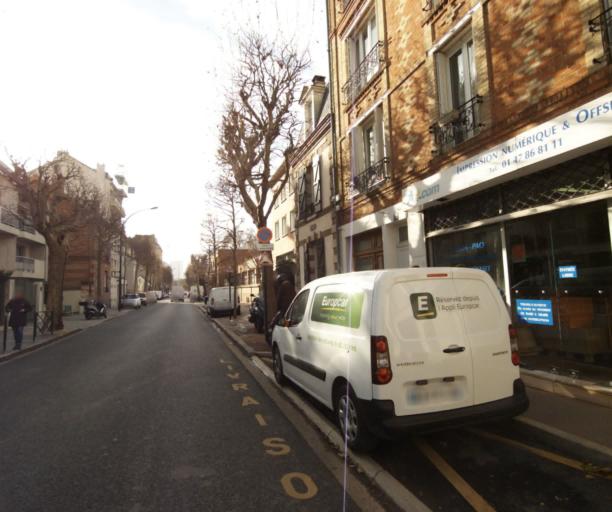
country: FR
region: Ile-de-France
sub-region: Departement des Hauts-de-Seine
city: La Garenne-Colombes
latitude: 48.9077
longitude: 2.2500
